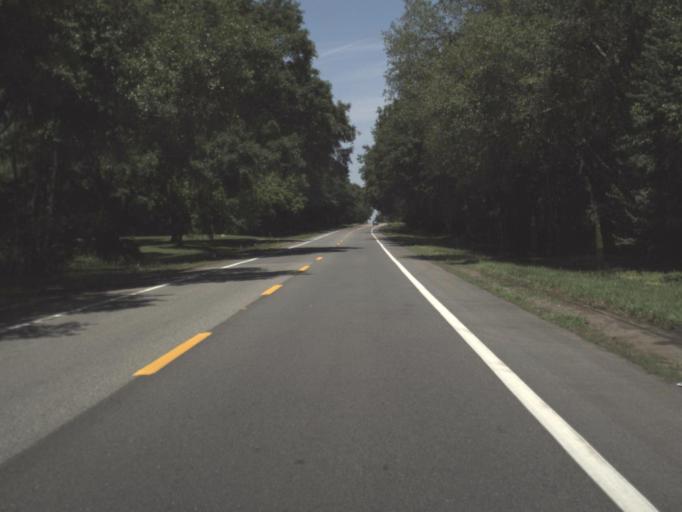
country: US
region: Florida
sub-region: Suwannee County
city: Live Oak
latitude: 30.3334
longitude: -83.0681
